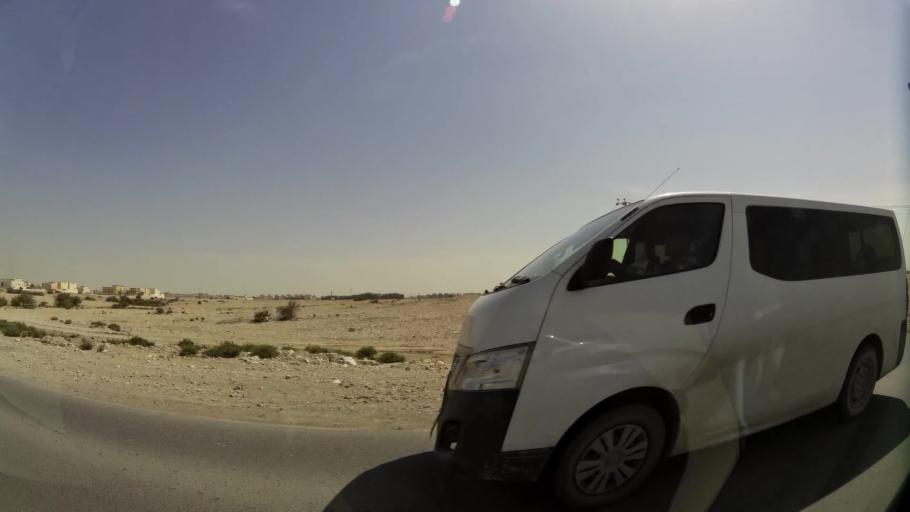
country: QA
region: Baladiyat ar Rayyan
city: Ar Rayyan
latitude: 25.2641
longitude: 51.4026
